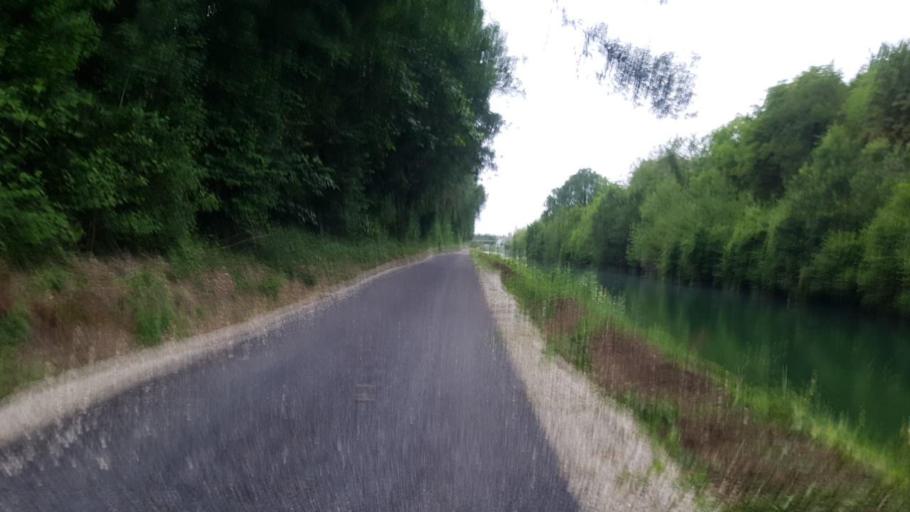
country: FR
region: Champagne-Ardenne
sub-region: Departement de la Marne
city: Sarry
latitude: 48.8426
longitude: 4.4985
